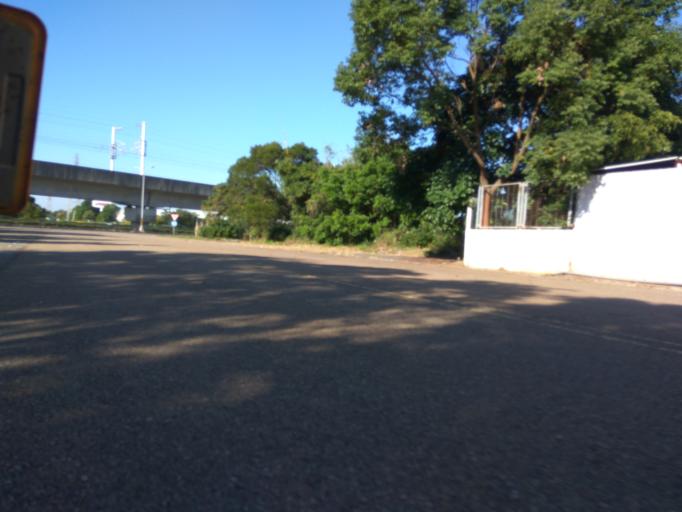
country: TW
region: Taiwan
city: Taoyuan City
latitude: 24.9724
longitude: 121.1759
